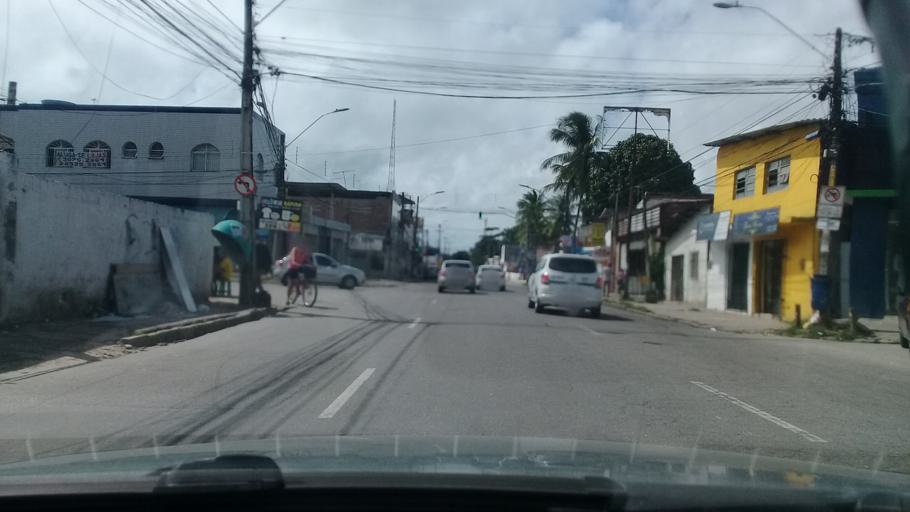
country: BR
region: Pernambuco
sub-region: Jaboatao Dos Guararapes
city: Jaboatao
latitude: -8.1636
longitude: -34.9236
